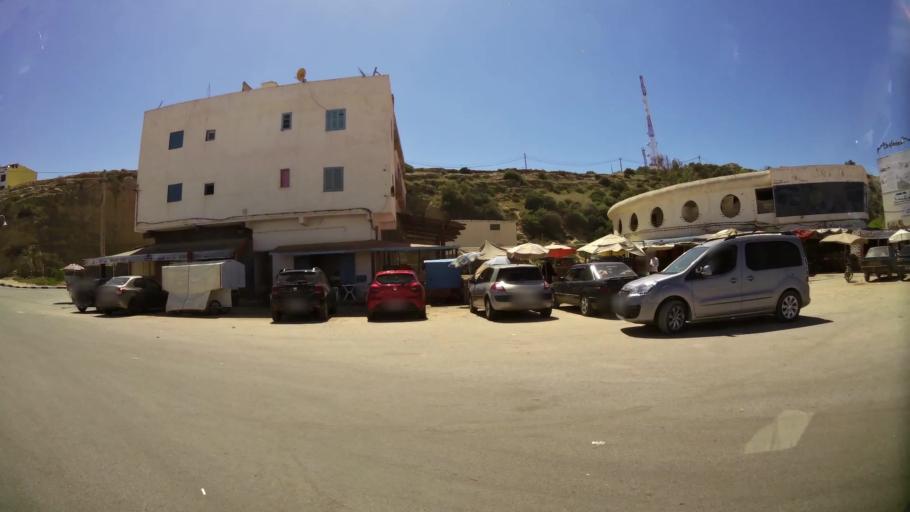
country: MA
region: Oriental
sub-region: Berkane-Taourirt
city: Madagh
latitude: 35.1411
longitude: -2.4241
